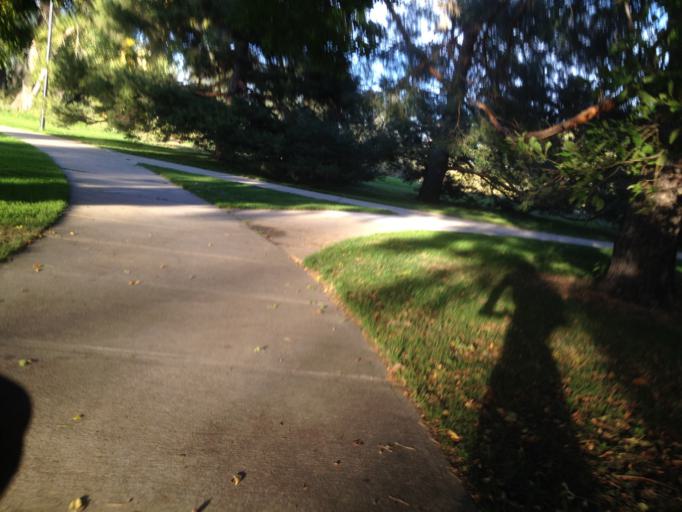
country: US
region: Colorado
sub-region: Boulder County
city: Louisville
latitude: 39.9852
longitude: -105.1415
